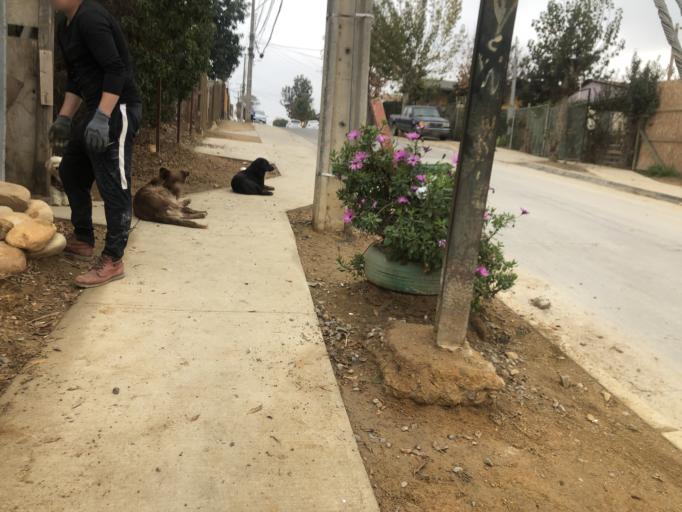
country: CL
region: Valparaiso
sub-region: Provincia de Marga Marga
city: Quilpue
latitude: -33.0503
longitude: -71.4267
